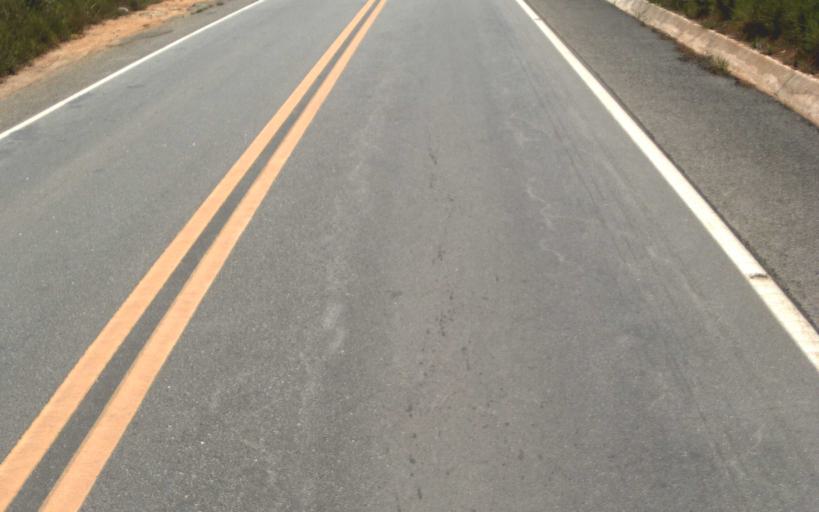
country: BR
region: Minas Gerais
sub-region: Governador Valadares
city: Governador Valadares
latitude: -18.9891
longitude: -42.1123
